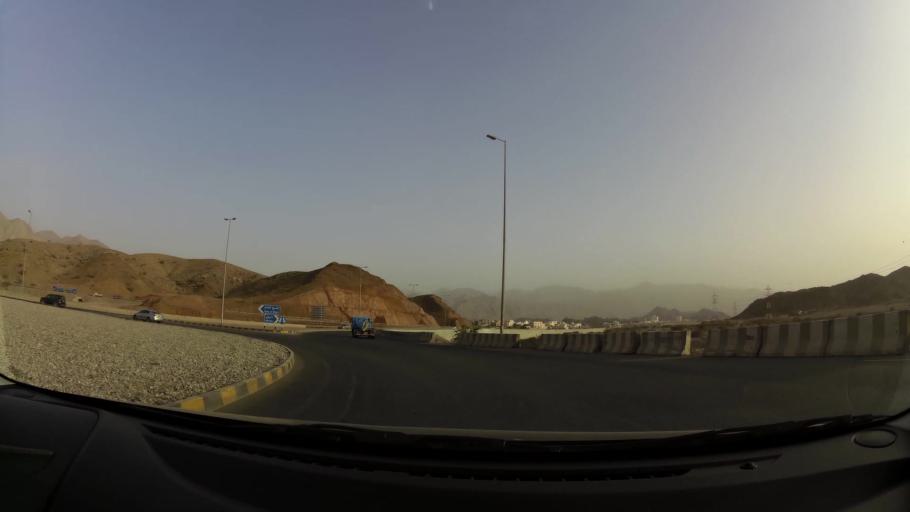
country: OM
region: Muhafazat Masqat
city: Bawshar
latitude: 23.5203
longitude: 58.3469
